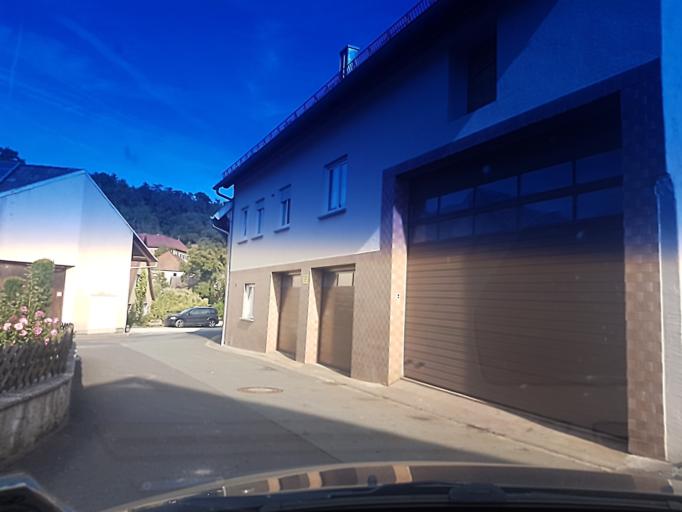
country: DE
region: Bavaria
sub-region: Regierungsbezirk Mittelfranken
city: Burghaslach
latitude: 49.7731
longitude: 10.5616
